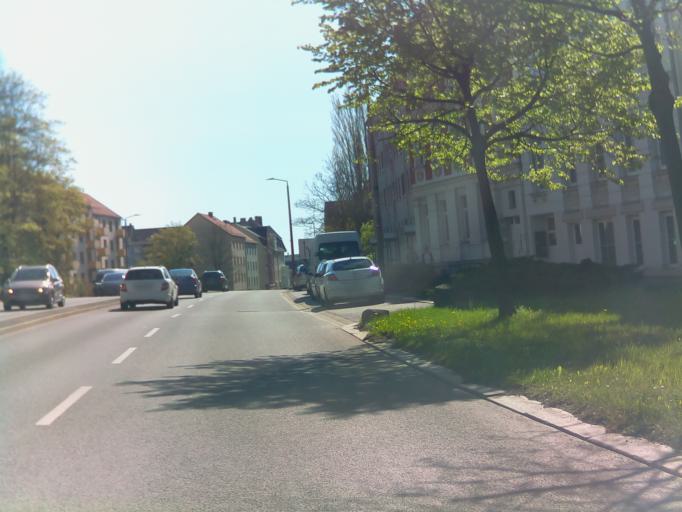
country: DE
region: Saxony
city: Plauen
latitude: 50.5074
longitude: 12.1323
